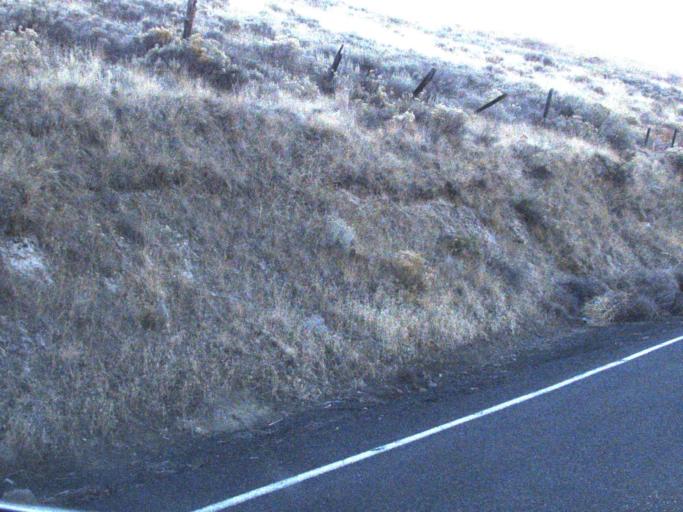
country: US
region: Washington
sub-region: Adams County
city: Ritzville
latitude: 46.6974
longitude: -118.3917
